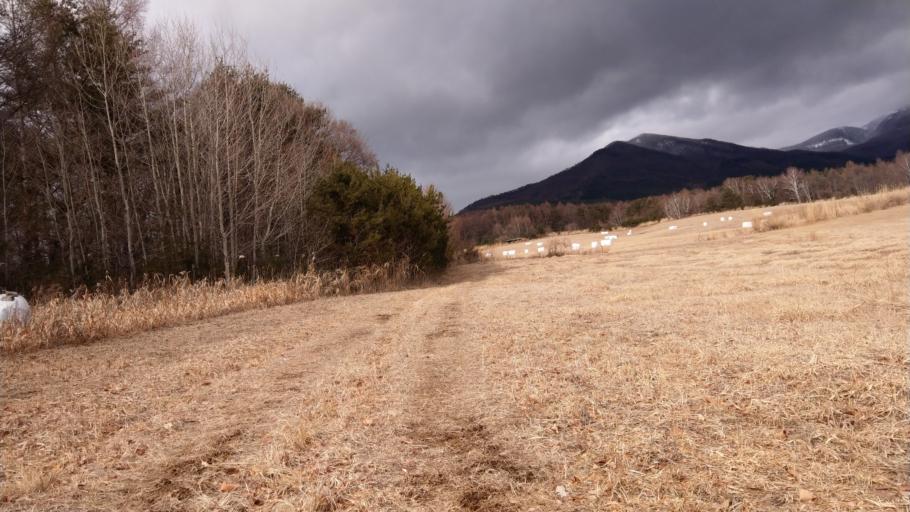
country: JP
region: Nagano
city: Komoro
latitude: 36.3649
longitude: 138.4376
